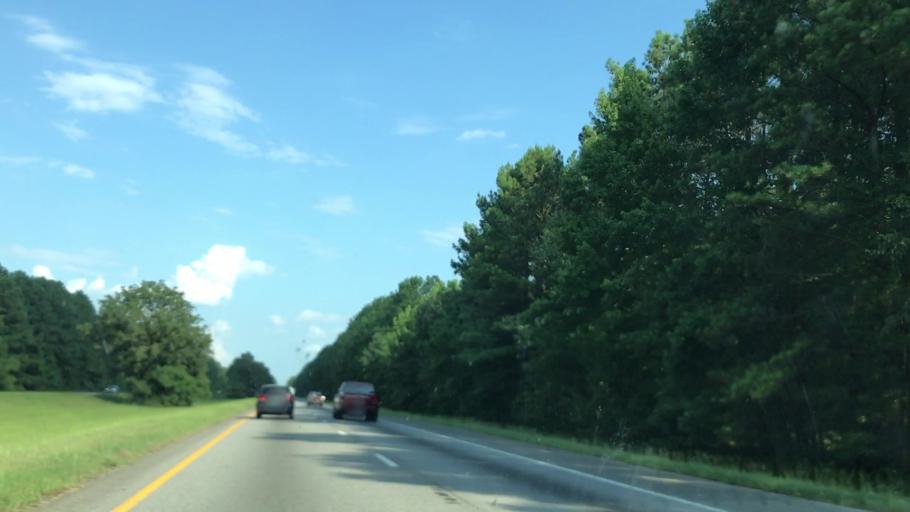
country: US
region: South Carolina
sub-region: Dorchester County
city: Saint George
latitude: 33.3773
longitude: -80.6181
